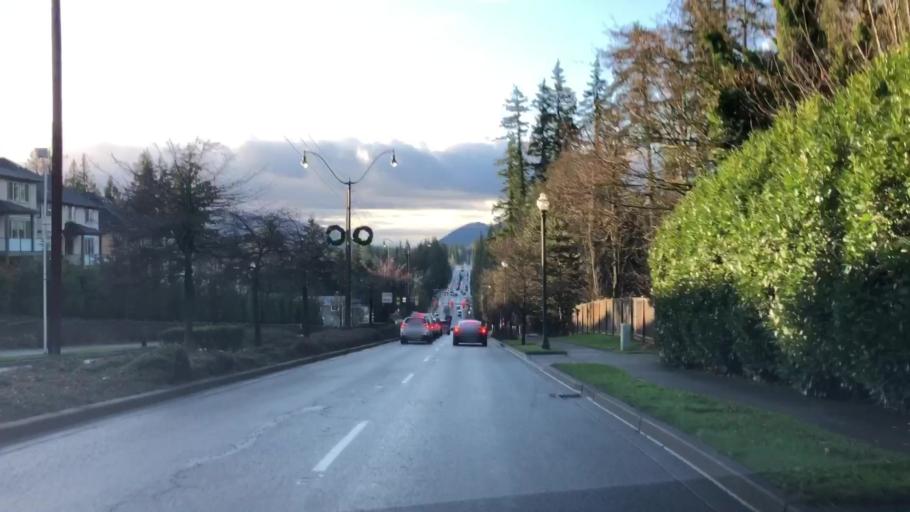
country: US
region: Washington
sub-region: King County
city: City of Sammamish
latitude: 47.5933
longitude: -122.0356
